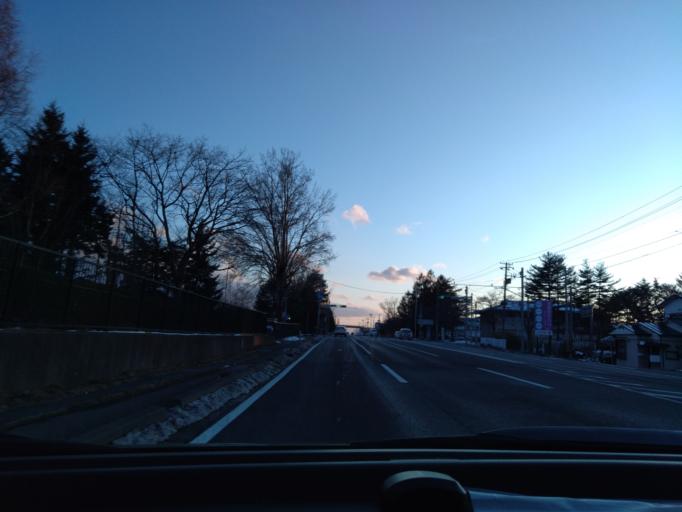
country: JP
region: Iwate
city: Hanamaki
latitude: 39.4256
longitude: 141.1302
